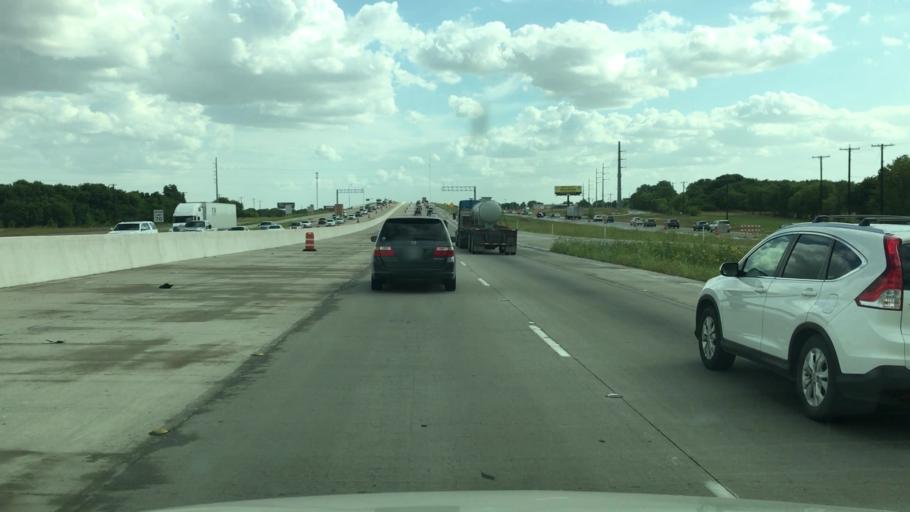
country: US
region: Texas
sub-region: McLennan County
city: Bruceville-Eddy
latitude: 31.3133
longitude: -97.2413
